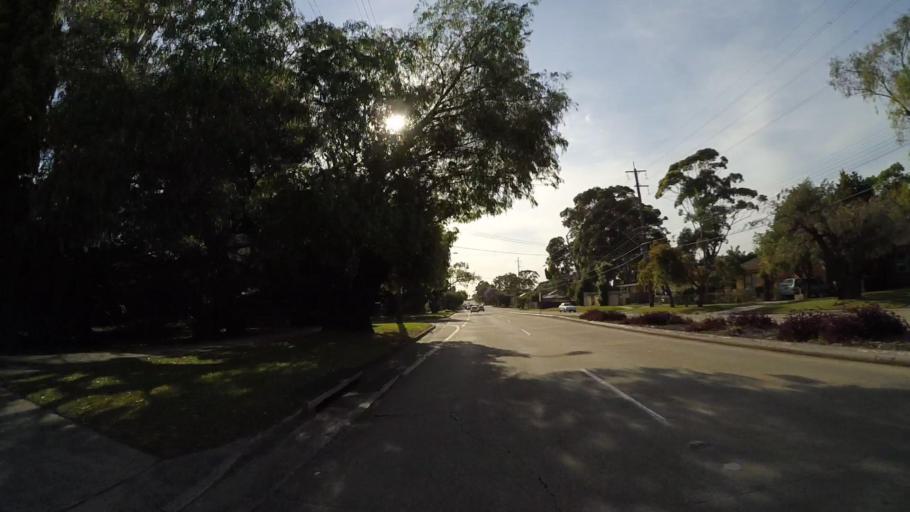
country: AU
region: New South Wales
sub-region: Sutherland Shire
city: Gymea
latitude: -34.0277
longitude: 151.0909
